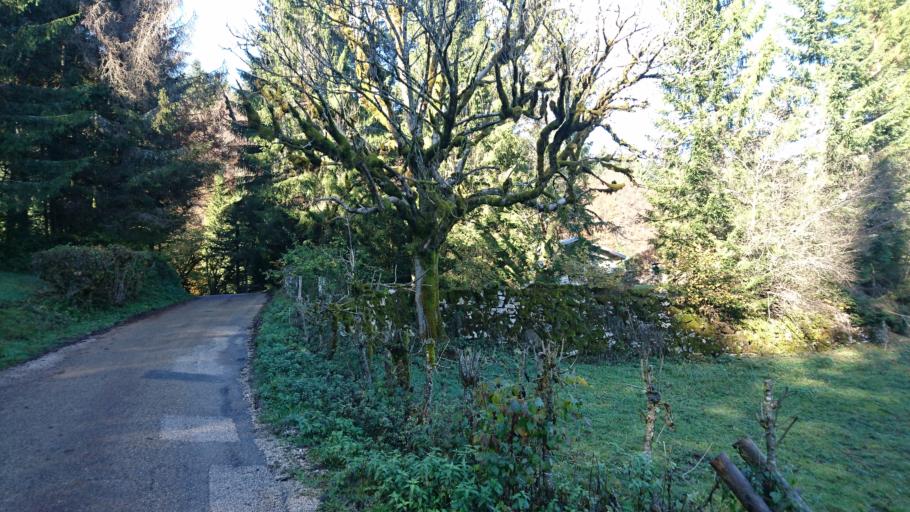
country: FR
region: Rhone-Alpes
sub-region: Departement de l'Ain
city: Oyonnax
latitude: 46.2210
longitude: 5.6939
